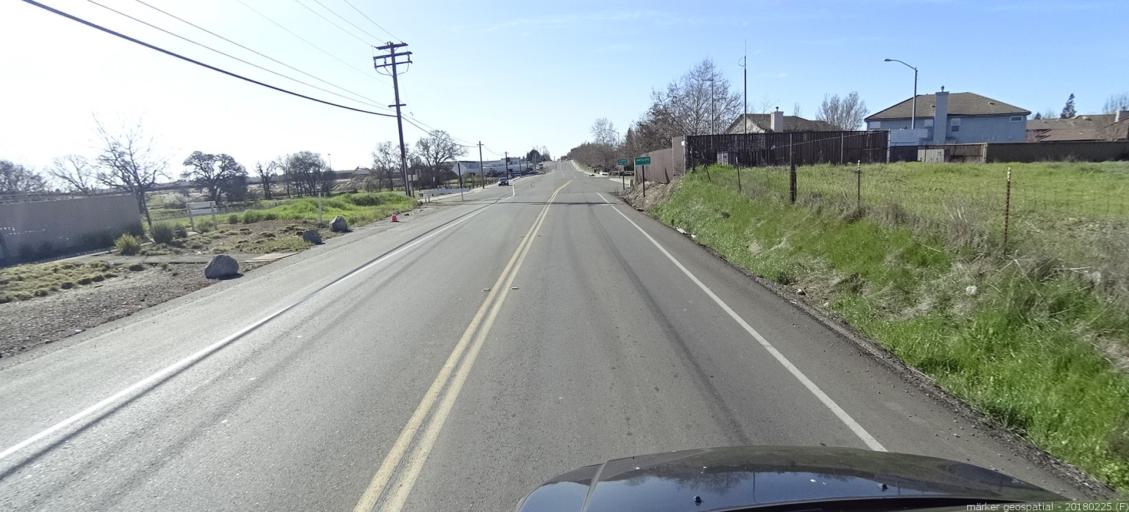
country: US
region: California
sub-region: Sacramento County
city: Antelope
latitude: 38.7246
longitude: -121.3275
